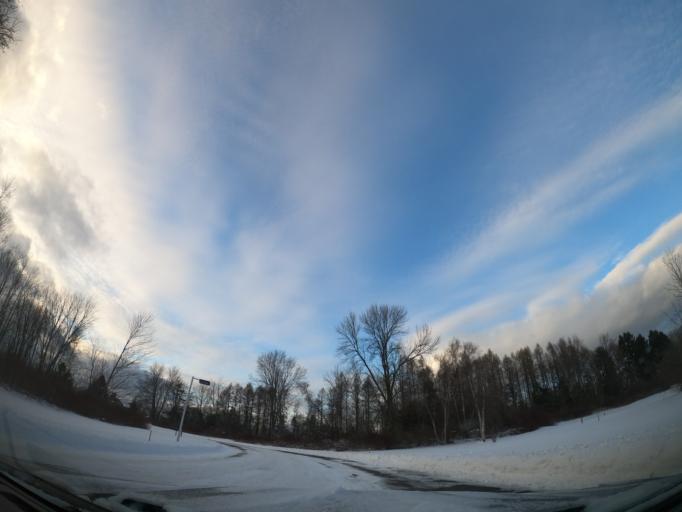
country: US
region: New York
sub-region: Onondaga County
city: Brewerton
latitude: 43.2271
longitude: -76.1109
